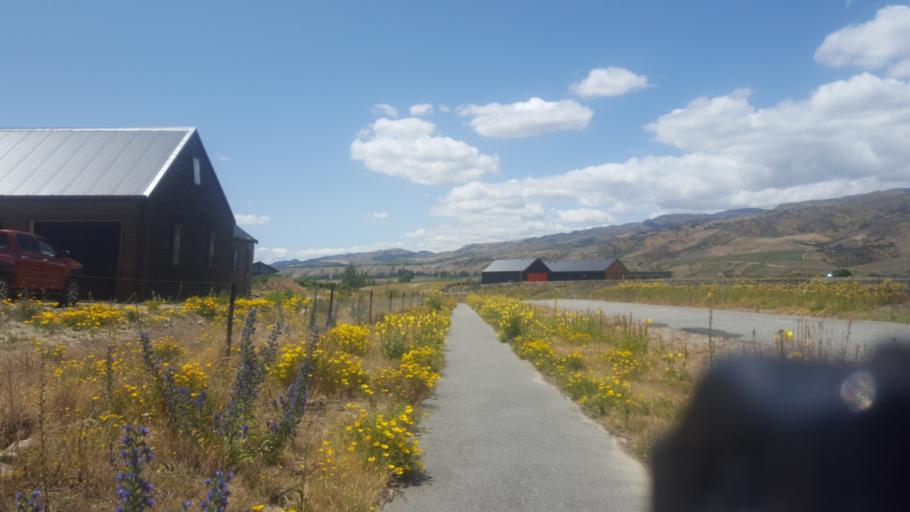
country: NZ
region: Otago
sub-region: Queenstown-Lakes District
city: Wanaka
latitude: -45.0302
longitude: 169.2047
